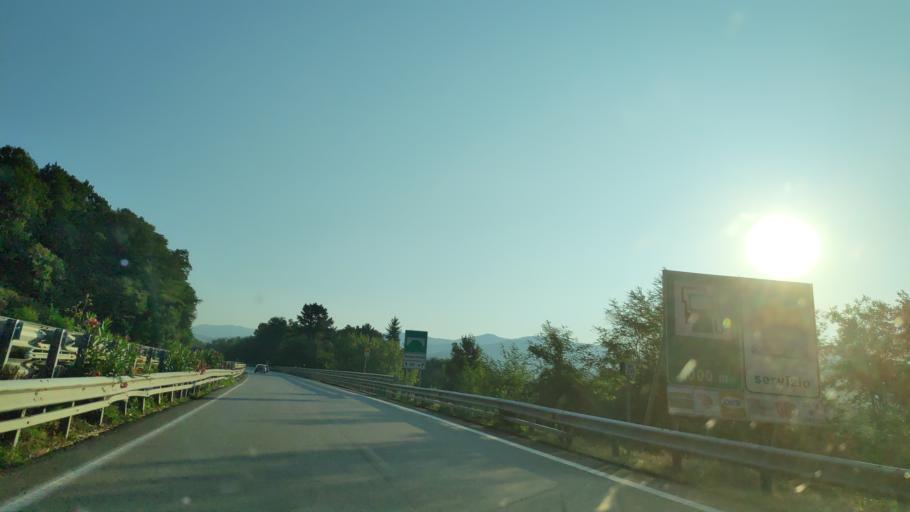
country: IT
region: Calabria
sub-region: Provincia di Cosenza
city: Marzi
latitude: 39.1795
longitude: 16.2996
